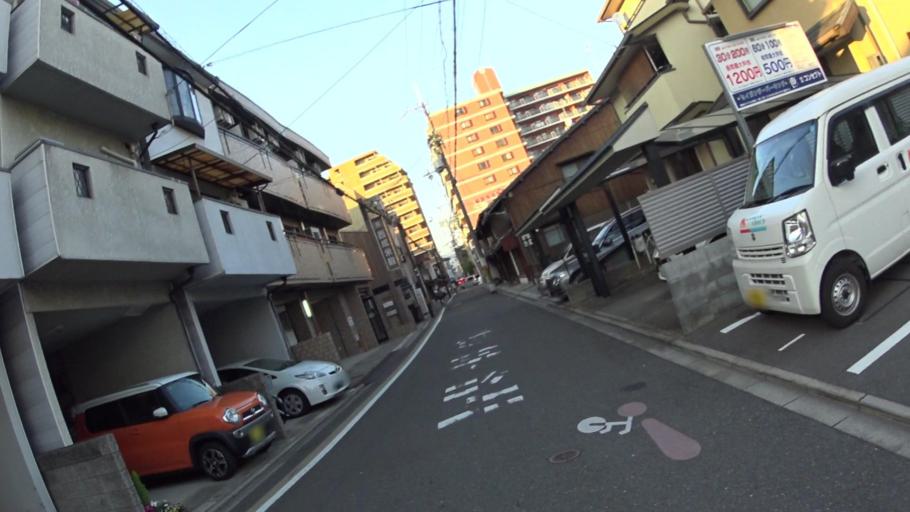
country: JP
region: Kyoto
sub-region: Kyoto-shi
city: Kamigyo-ku
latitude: 35.0287
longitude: 135.7489
